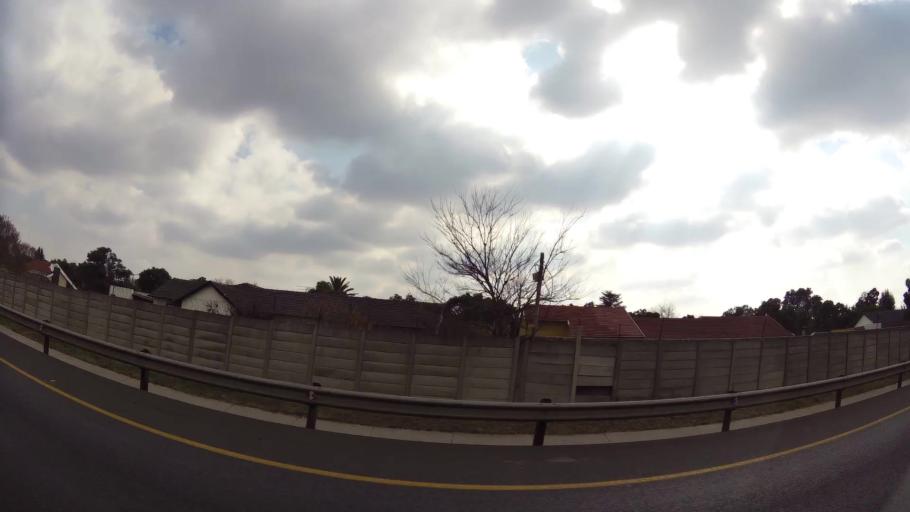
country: ZA
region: Gauteng
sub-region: Ekurhuleni Metropolitan Municipality
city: Benoni
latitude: -26.1739
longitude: 28.3398
